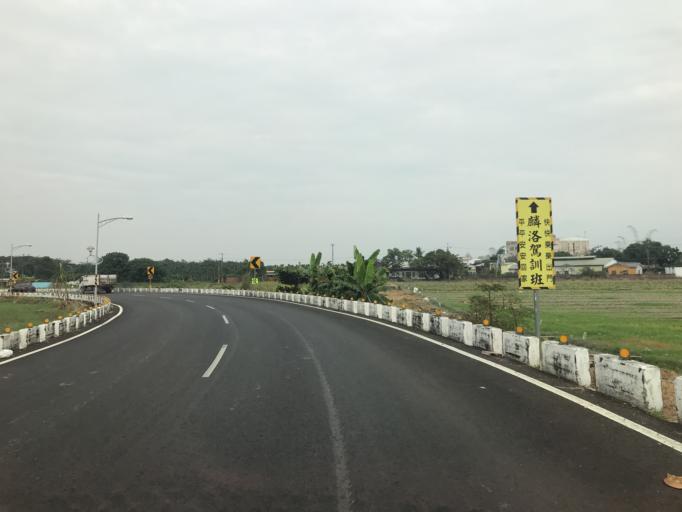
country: TW
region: Taiwan
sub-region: Pingtung
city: Pingtung
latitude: 22.6378
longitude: 120.5388
